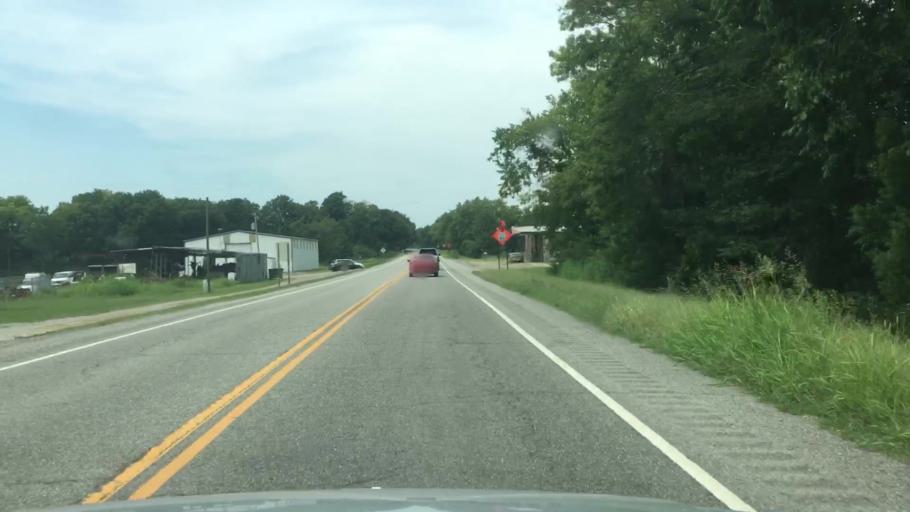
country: US
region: Oklahoma
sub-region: Muskogee County
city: Fort Gibson
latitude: 35.9342
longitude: -95.1579
